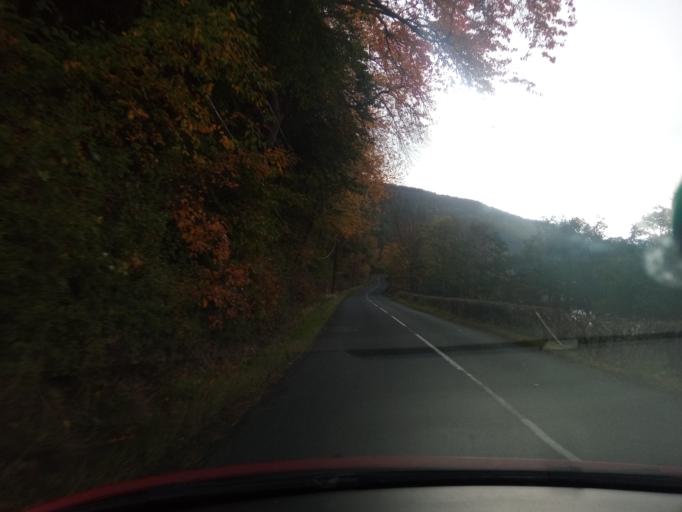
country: GB
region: Scotland
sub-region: The Scottish Borders
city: Selkirk
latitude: 55.6013
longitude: -2.8694
